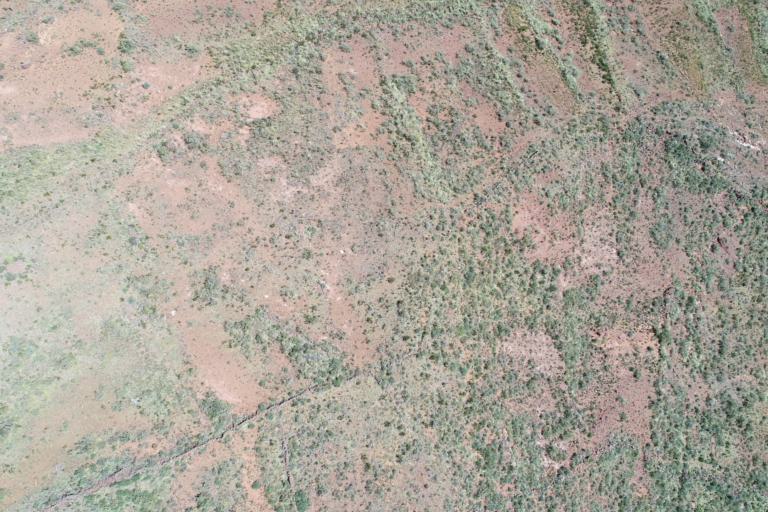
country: BO
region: La Paz
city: Tiahuanaco
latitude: -16.6050
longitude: -68.7707
